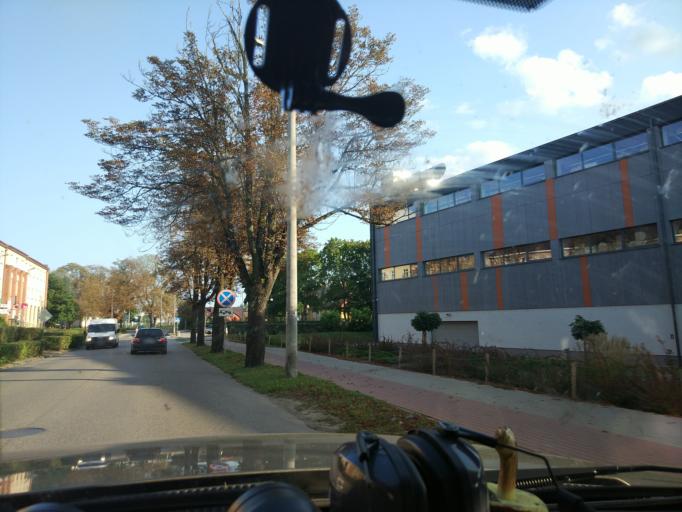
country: PL
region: Warmian-Masurian Voivodeship
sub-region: Powiat szczycienski
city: Szczytno
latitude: 53.5625
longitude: 20.9895
